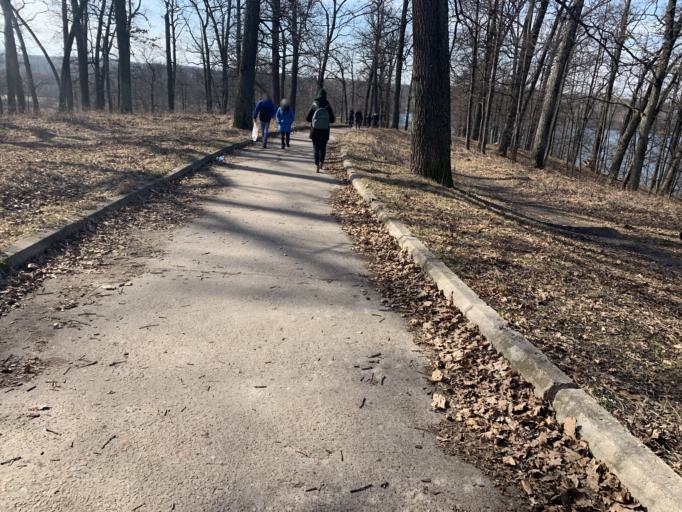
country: RU
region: Kursk
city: Zheleznogorsk
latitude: 52.3194
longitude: 35.3637
